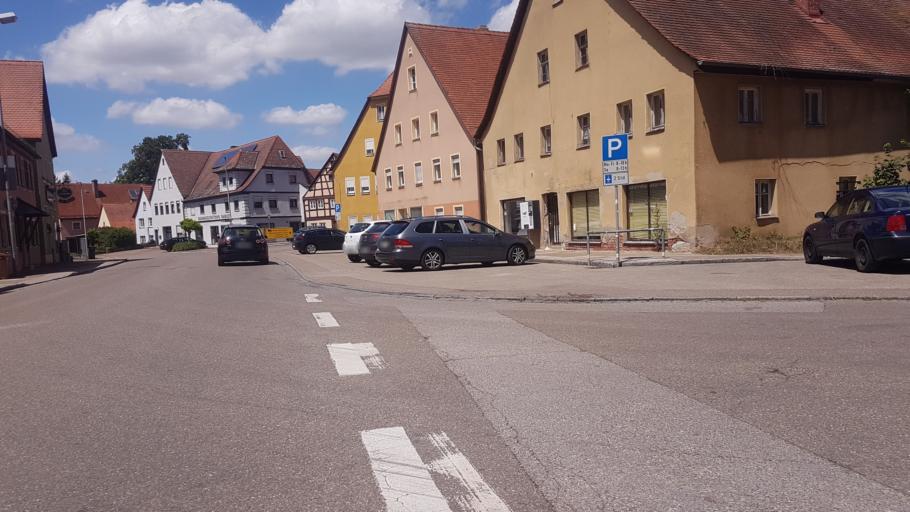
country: DE
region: Bavaria
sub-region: Regierungsbezirk Mittelfranken
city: Leutershausen
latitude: 49.3004
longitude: 10.4068
